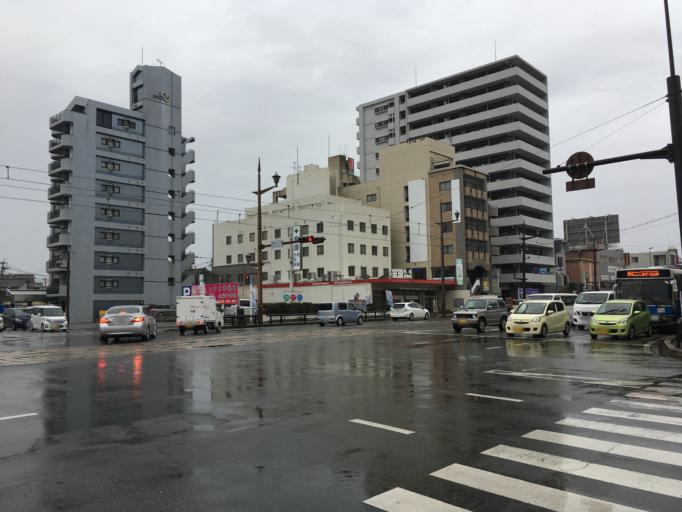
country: JP
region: Kumamoto
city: Kumamoto
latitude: 32.7929
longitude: 130.7282
